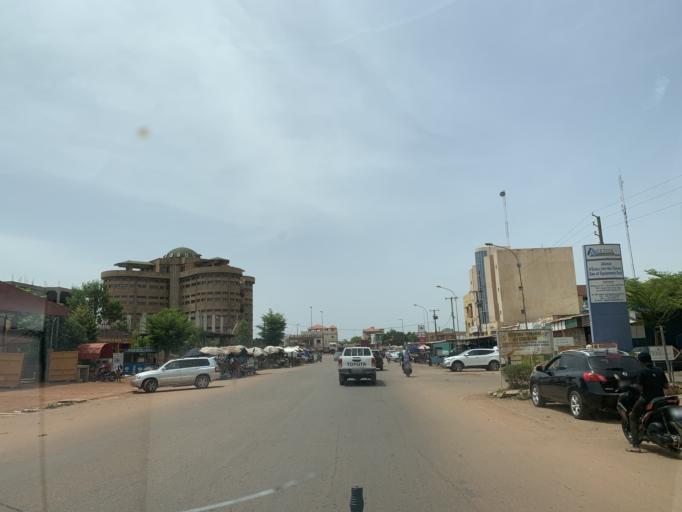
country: BF
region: Centre
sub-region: Kadiogo Province
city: Ouagadougou
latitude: 12.3364
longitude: -1.5001
